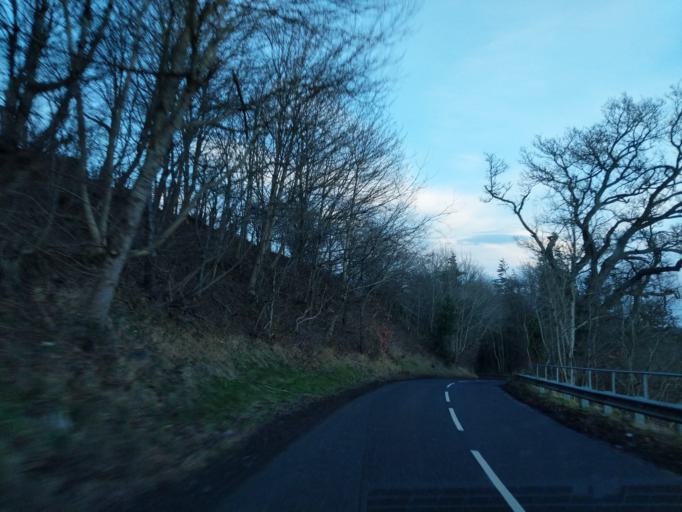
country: GB
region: Scotland
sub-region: Midlothian
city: Bonnyrigg
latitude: 55.8184
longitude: -3.0959
